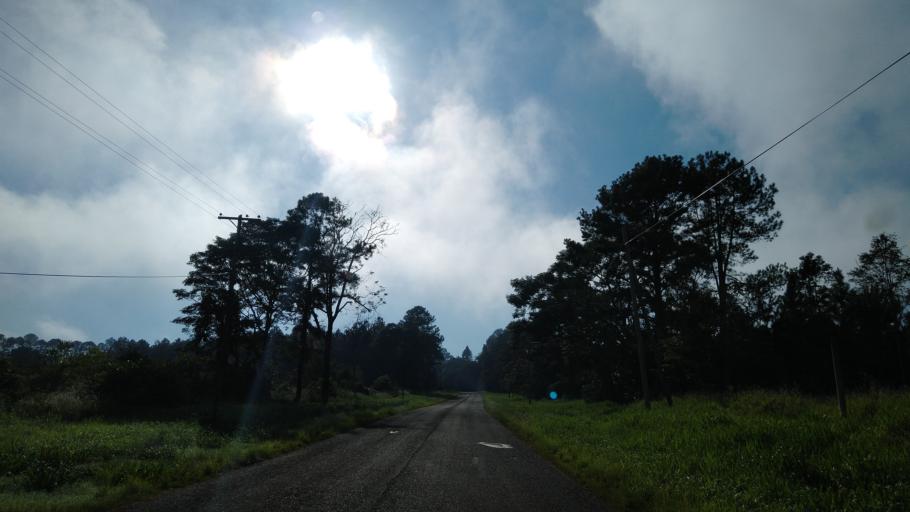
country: AR
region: Misiones
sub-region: Departamento de Montecarlo
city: Montecarlo
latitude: -26.5657
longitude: -54.7913
